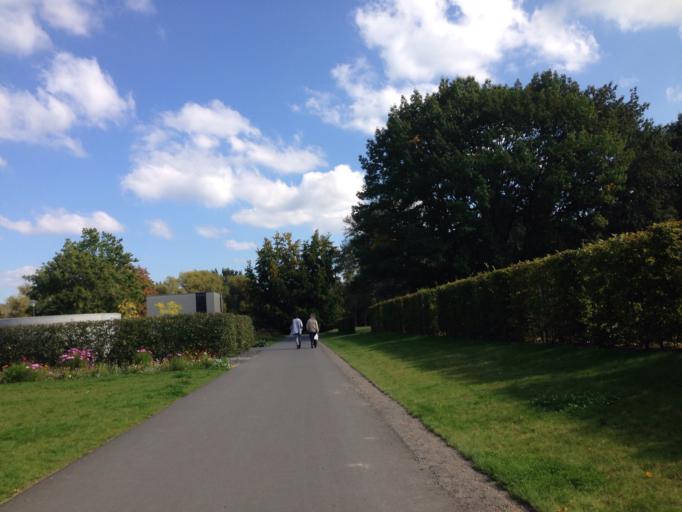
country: DE
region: Hesse
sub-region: Regierungsbezirk Giessen
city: Giessen
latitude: 50.5905
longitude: 8.6847
